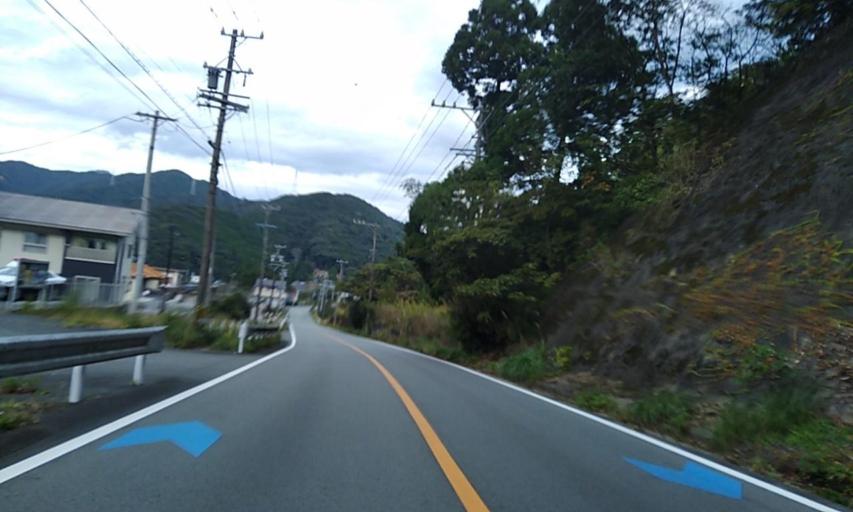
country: JP
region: Mie
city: Ise
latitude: 34.2742
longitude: 136.4919
